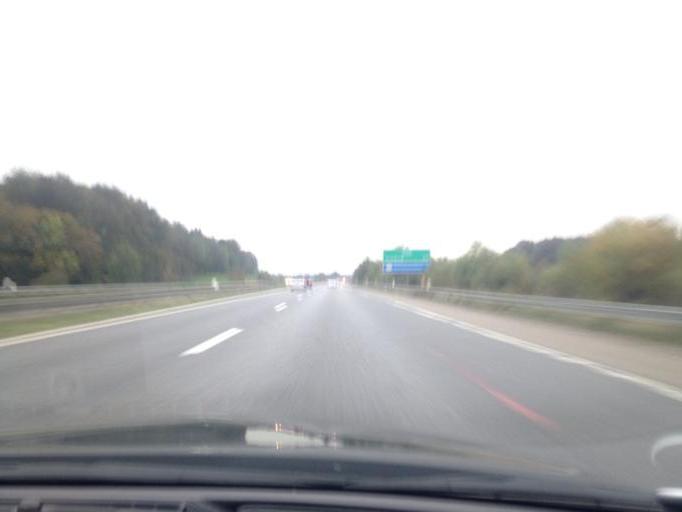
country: DK
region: South Denmark
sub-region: Haderslev Kommune
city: Haderslev
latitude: 55.3008
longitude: 9.4308
